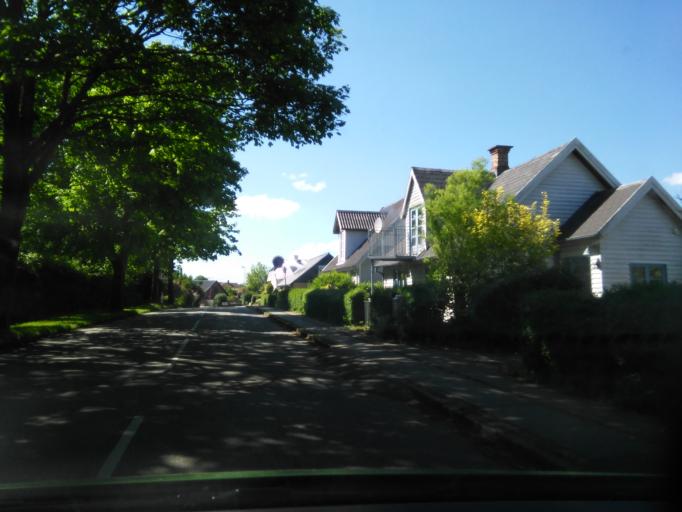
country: DK
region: Central Jutland
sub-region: Arhus Kommune
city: Malling
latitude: 56.0380
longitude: 10.1973
